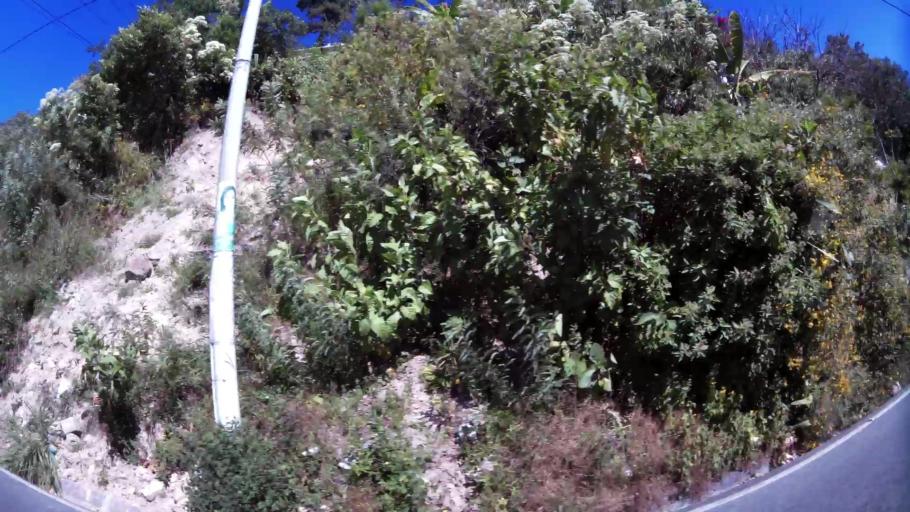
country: GT
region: Solola
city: Solola
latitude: 14.7537
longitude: -91.1718
